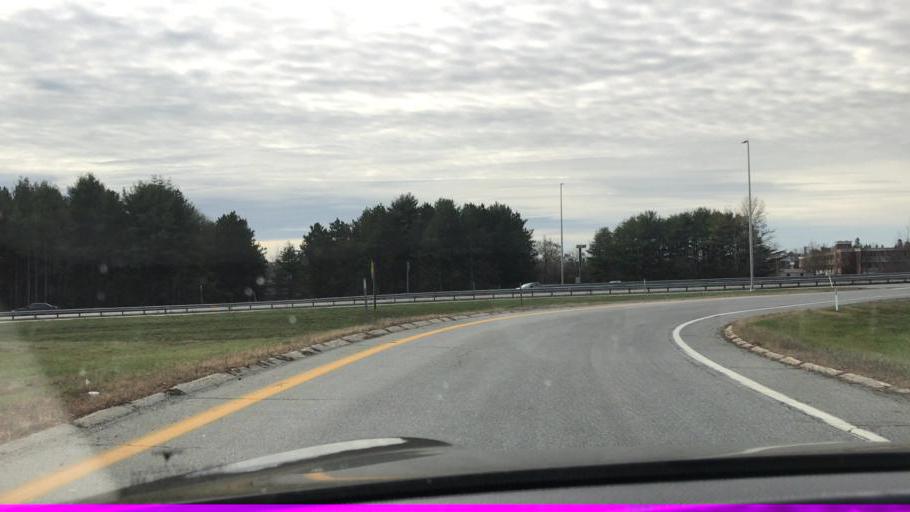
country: US
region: Maine
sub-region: Penobscot County
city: Bangor
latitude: 44.7882
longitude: -68.8106
